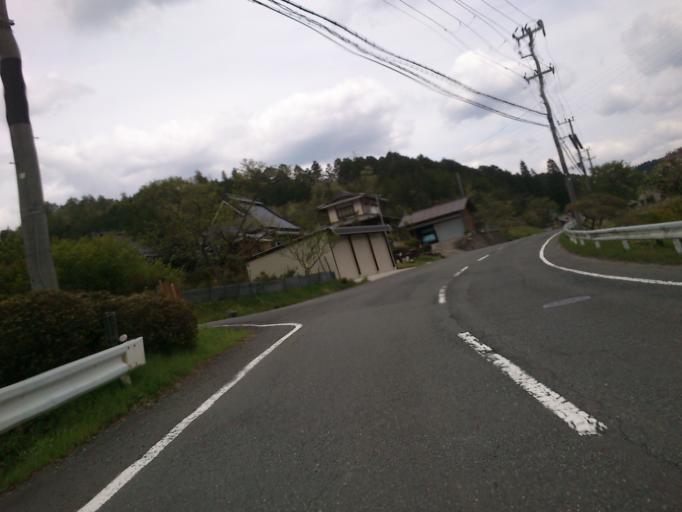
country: JP
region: Kyoto
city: Kameoka
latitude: 35.2073
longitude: 135.5940
